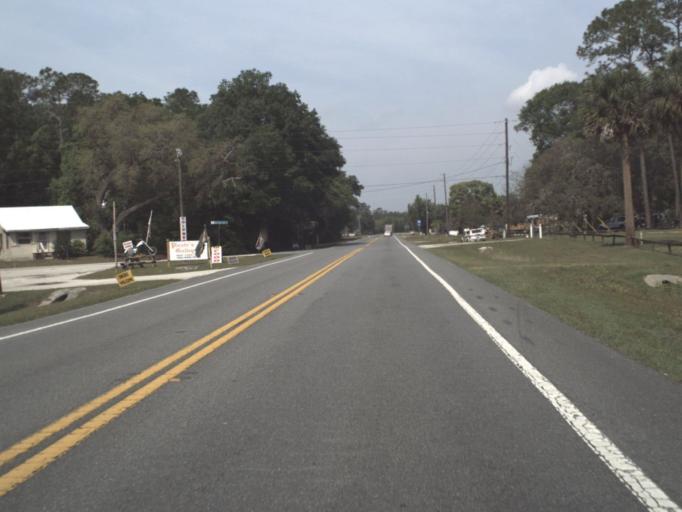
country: US
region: Florida
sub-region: Lake County
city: Astor
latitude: 29.1537
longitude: -81.5714
